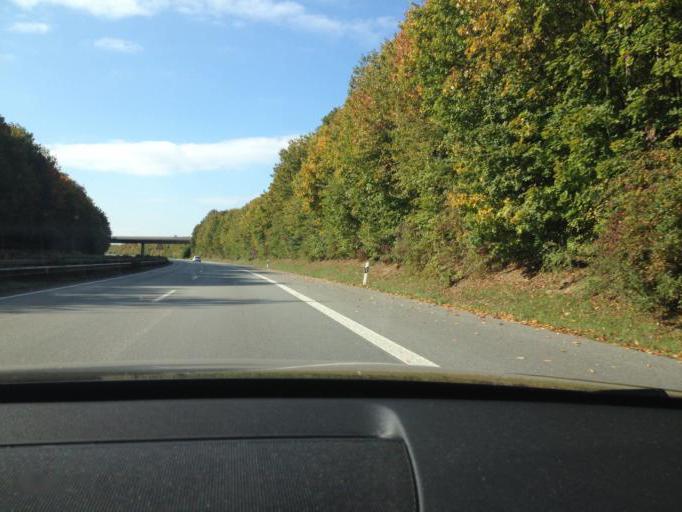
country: DE
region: Rheinland-Pfalz
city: Contwig
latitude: 49.2291
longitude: 7.4303
